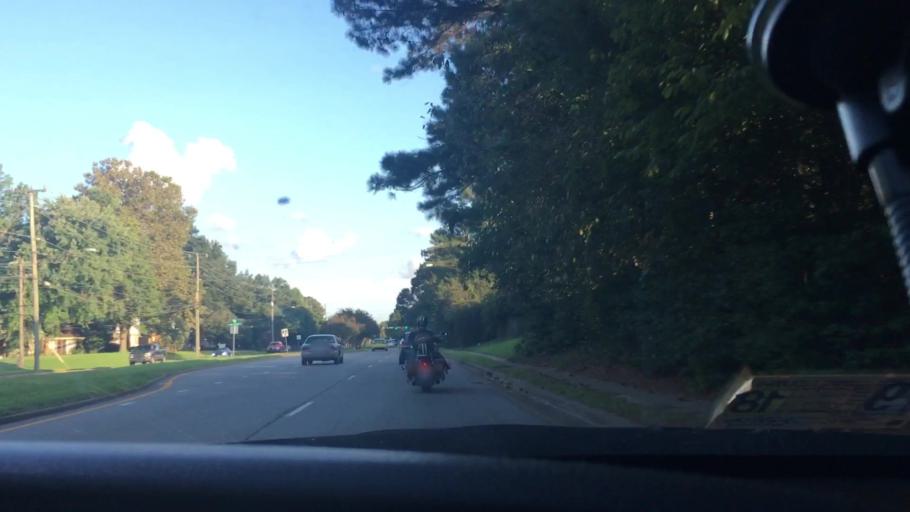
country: US
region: Virginia
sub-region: City of Norfolk
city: Norfolk
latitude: 36.8866
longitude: -76.1361
